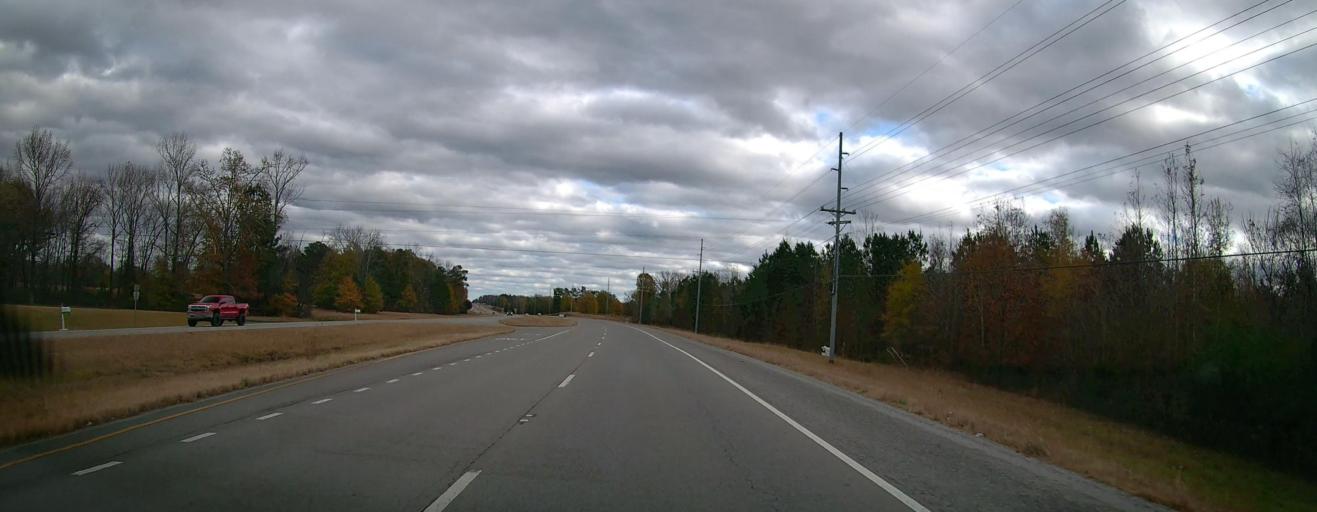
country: US
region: Alabama
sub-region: Lawrence County
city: Town Creek
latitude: 34.5755
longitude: -87.4017
